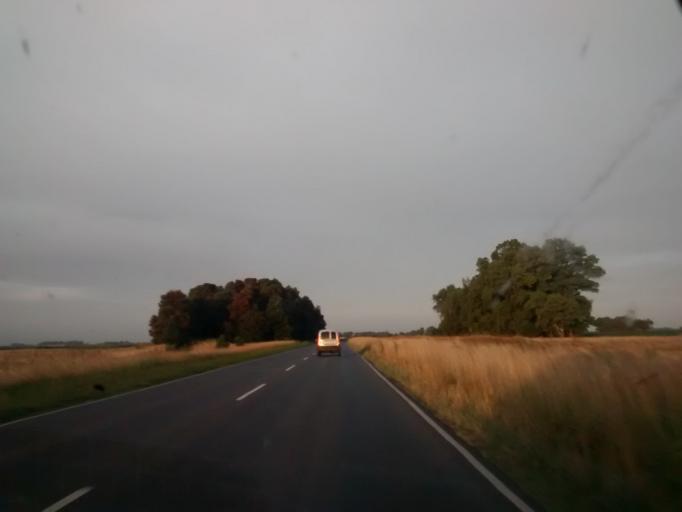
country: AR
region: Buenos Aires
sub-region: Partido de General Belgrano
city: General Belgrano
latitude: -35.8528
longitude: -58.6038
